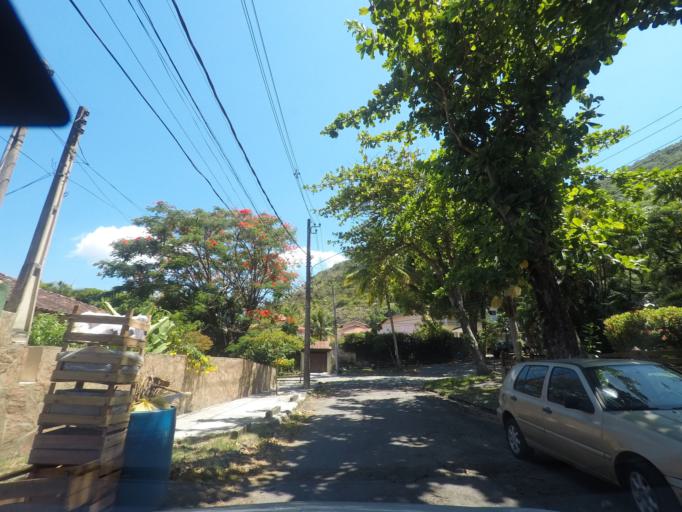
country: BR
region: Rio de Janeiro
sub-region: Niteroi
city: Niteroi
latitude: -22.9708
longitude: -43.0304
